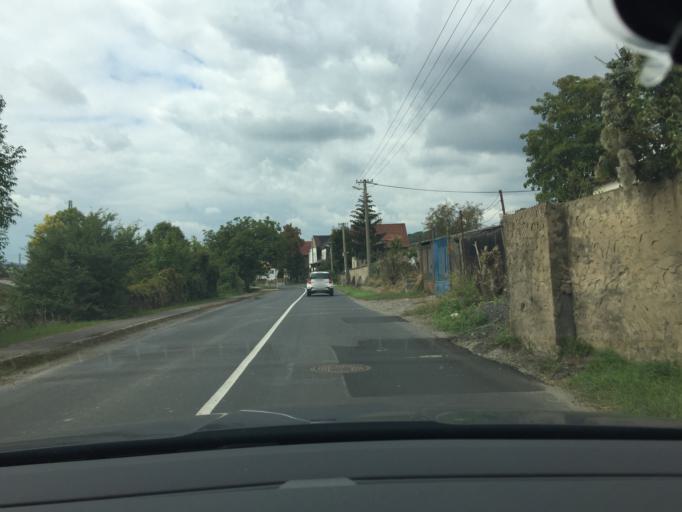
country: CZ
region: Ustecky
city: Lovosice
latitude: 50.5255
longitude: 14.0826
